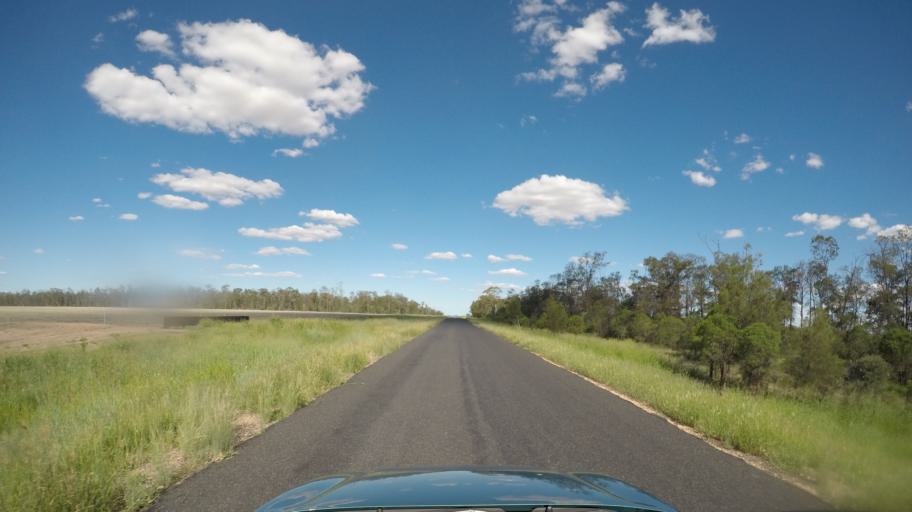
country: AU
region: Queensland
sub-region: Goondiwindi
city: Goondiwindi
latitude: -28.1723
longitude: 150.2298
